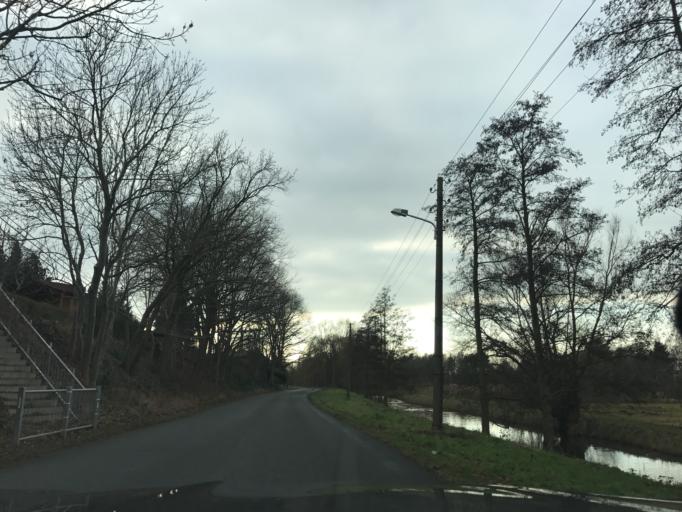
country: DE
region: Brandenburg
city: Brandenburg an der Havel
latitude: 52.3658
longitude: 12.5467
